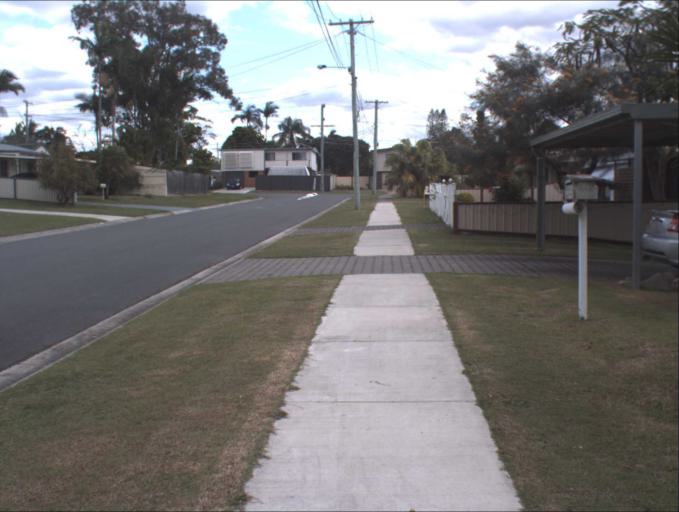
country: AU
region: Queensland
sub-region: Logan
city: Logan Reserve
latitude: -27.6839
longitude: 153.0871
